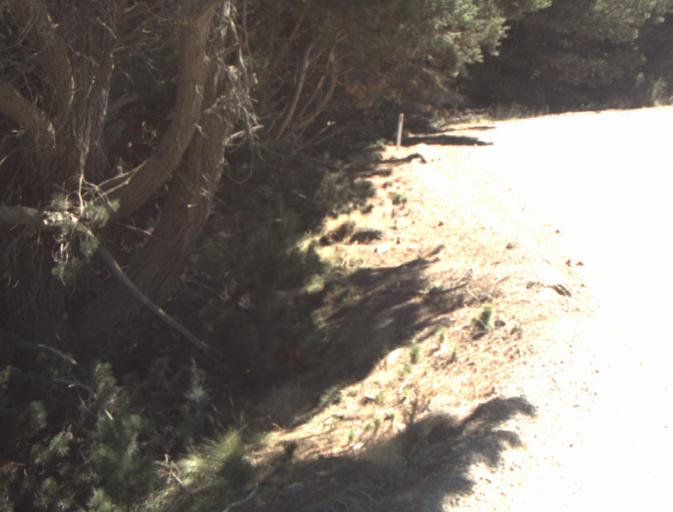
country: AU
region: Tasmania
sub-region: Dorset
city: Scottsdale
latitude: -41.3577
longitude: 147.4602
